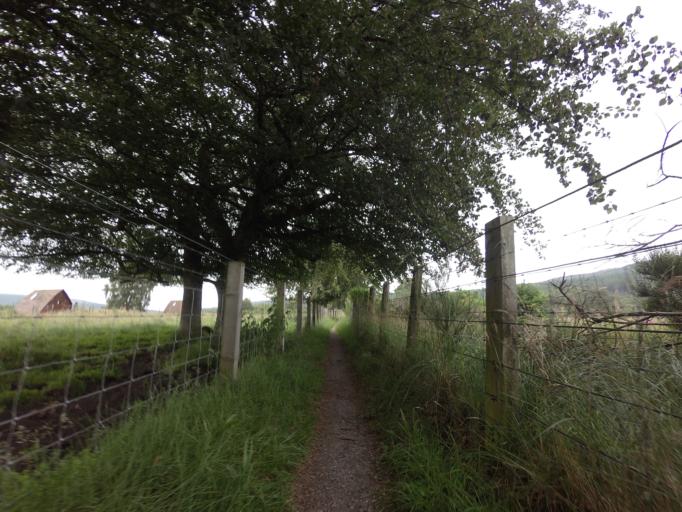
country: GB
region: Scotland
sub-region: Highland
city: Evanton
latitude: 57.9224
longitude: -4.4038
